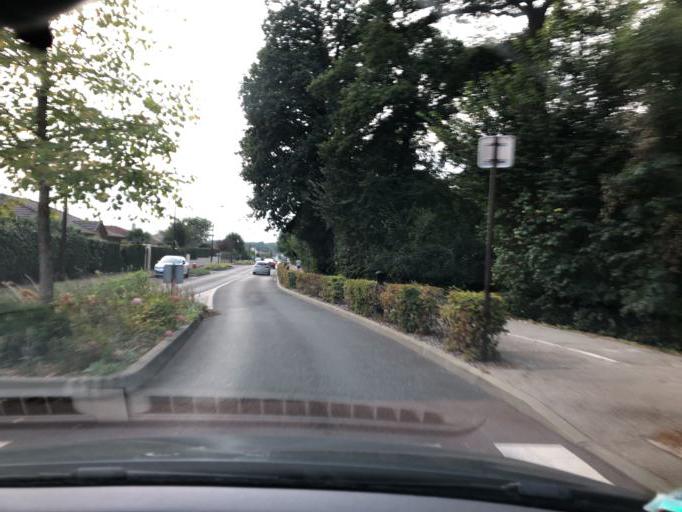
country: FR
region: Ile-de-France
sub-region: Departement des Yvelines
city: Velizy-Villacoublay
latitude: 48.7870
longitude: 2.1865
